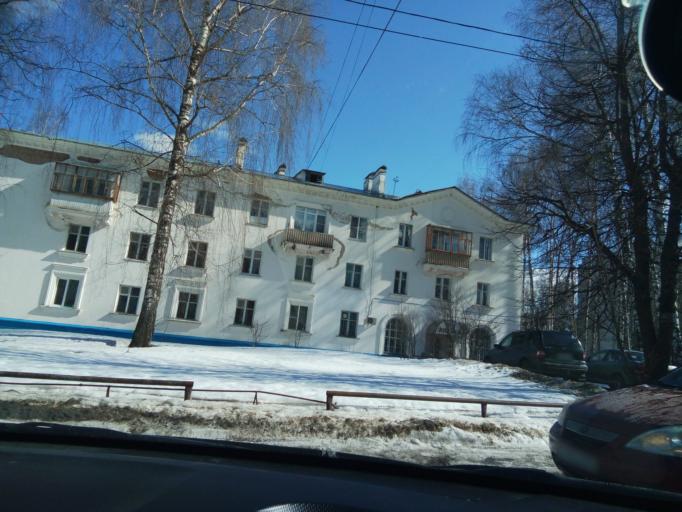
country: RU
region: Chuvashia
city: Novyye Lapsary
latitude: 56.1090
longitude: 47.1729
